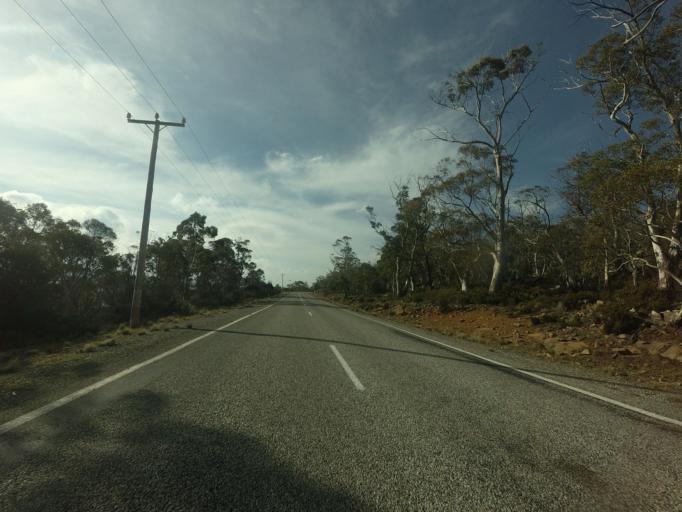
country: AU
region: Tasmania
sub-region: Meander Valley
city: Deloraine
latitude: -41.9881
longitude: 146.7101
